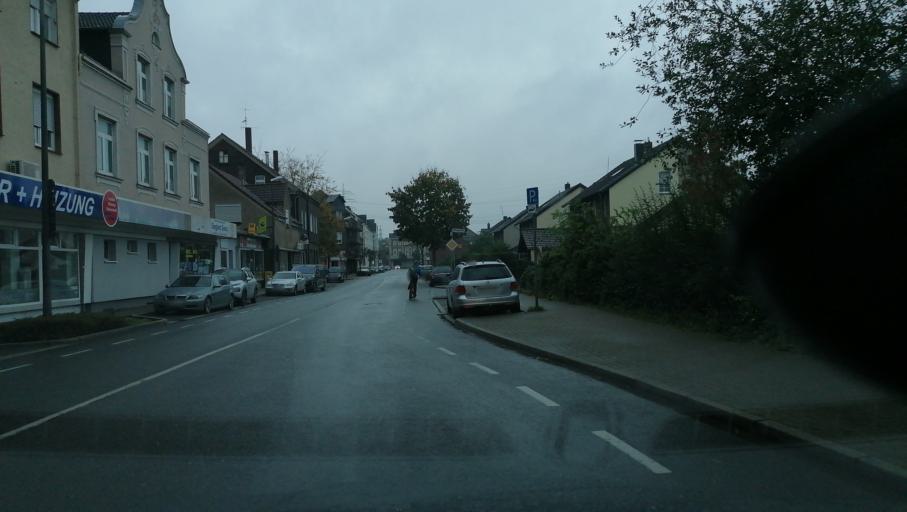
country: DE
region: North Rhine-Westphalia
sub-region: Regierungsbezirk Arnsberg
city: Herne
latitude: 51.5610
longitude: 7.1870
